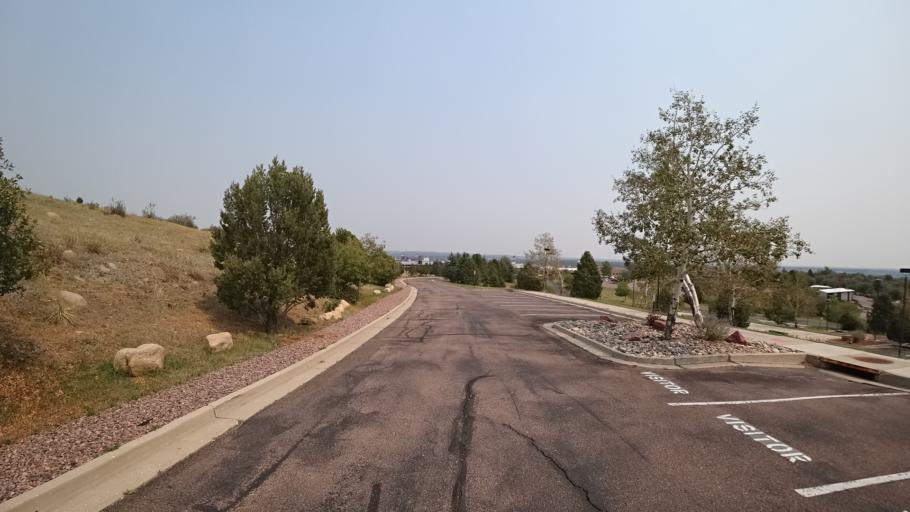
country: US
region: Colorado
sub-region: El Paso County
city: Colorado Springs
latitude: 38.8145
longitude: -104.8433
